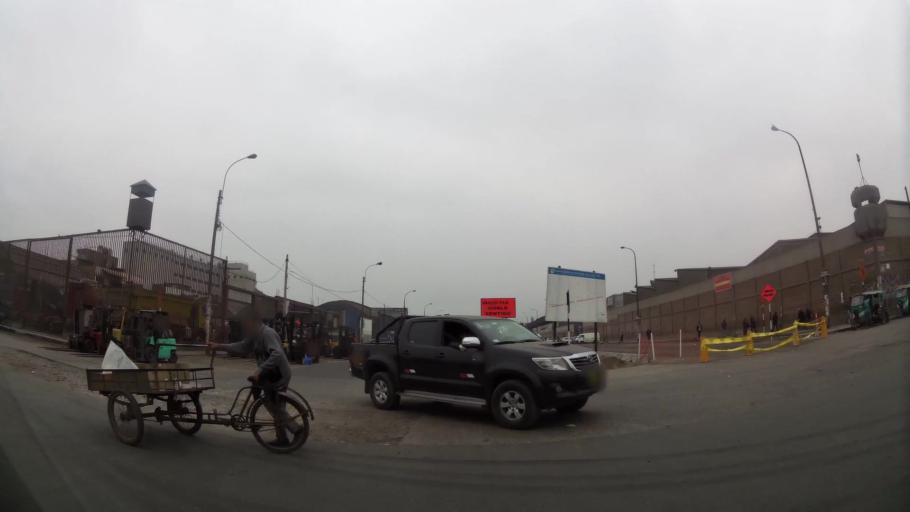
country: PE
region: Lima
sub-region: Lima
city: Vitarte
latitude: -12.0511
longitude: -76.9563
